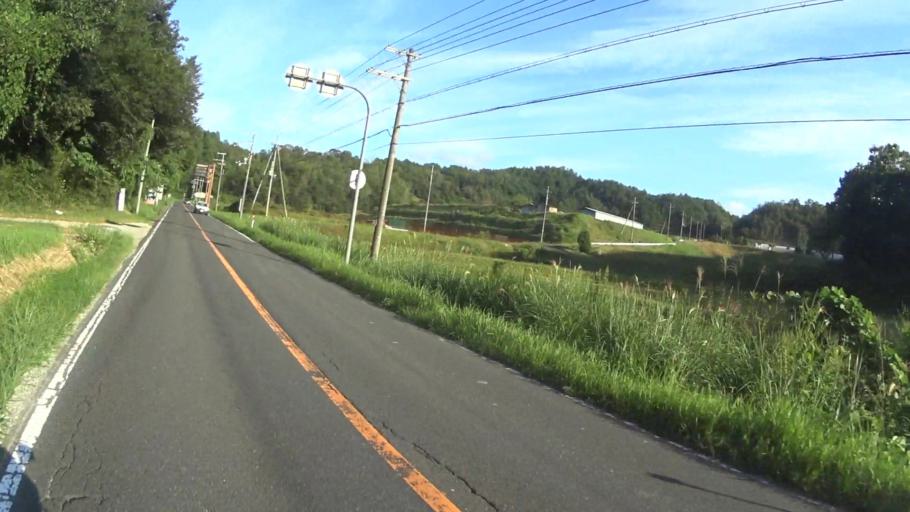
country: JP
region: Hyogo
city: Toyooka
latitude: 35.5946
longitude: 134.9091
